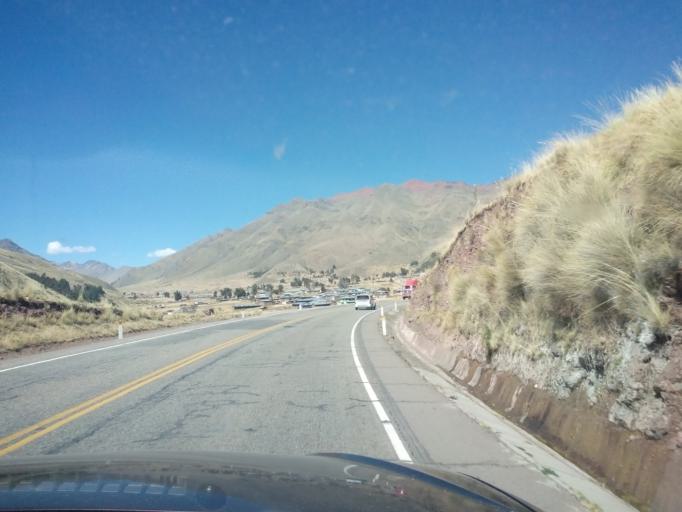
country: PE
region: Cusco
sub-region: Provincia de Canchis
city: Marangani
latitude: -14.4107
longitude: -71.1182
